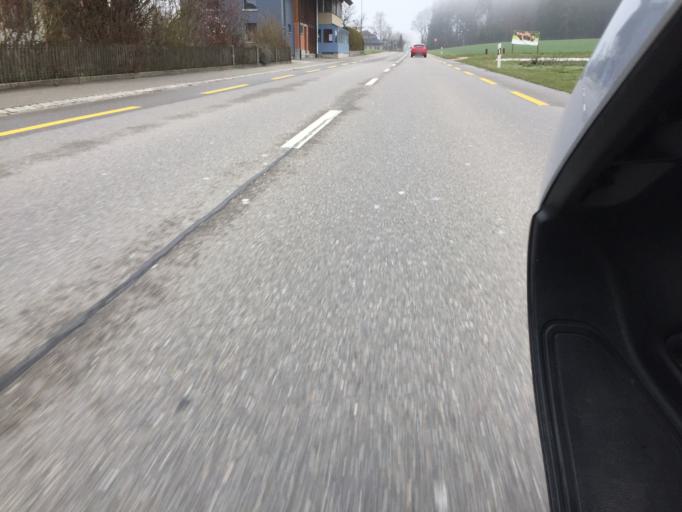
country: CH
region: Bern
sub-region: Seeland District
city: Schupfen
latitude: 47.0603
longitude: 7.4133
